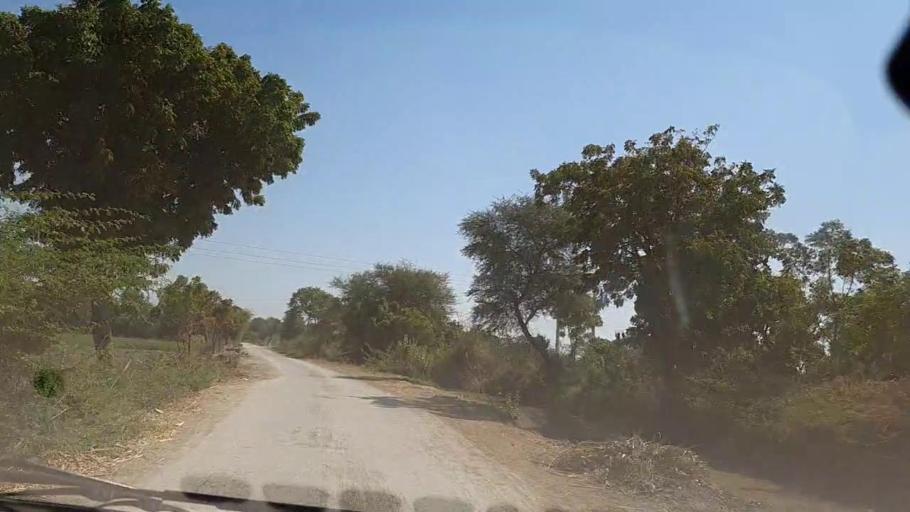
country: PK
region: Sindh
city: Mirpur Khas
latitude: 25.4307
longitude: 69.0211
